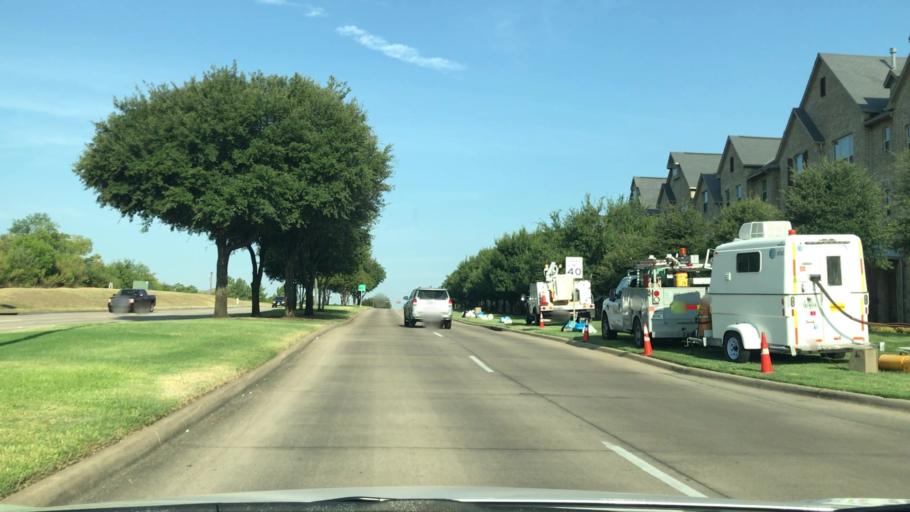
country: US
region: Texas
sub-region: Dallas County
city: Farmers Branch
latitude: 32.8959
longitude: -96.9525
